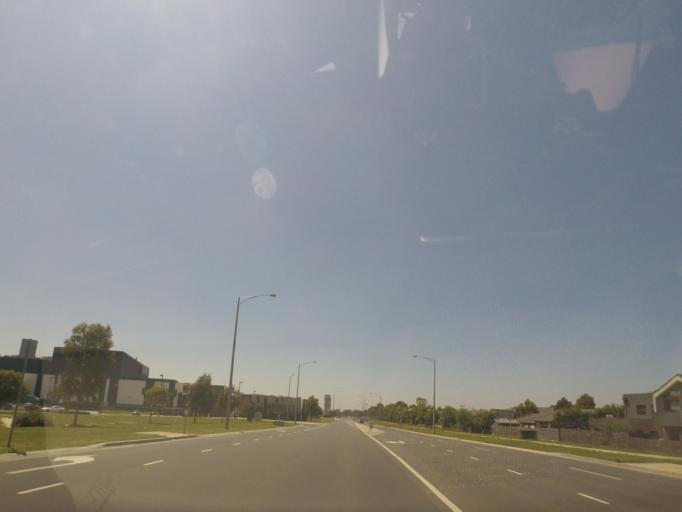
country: AU
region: Victoria
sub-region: Hume
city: Roxburgh Park
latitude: -37.5941
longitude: 144.9107
